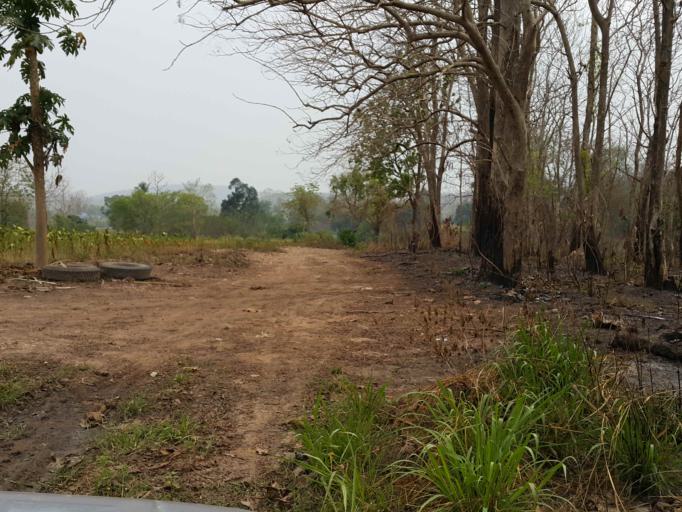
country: TH
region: Chiang Mai
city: Mae Taeng
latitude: 19.1161
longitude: 98.9881
